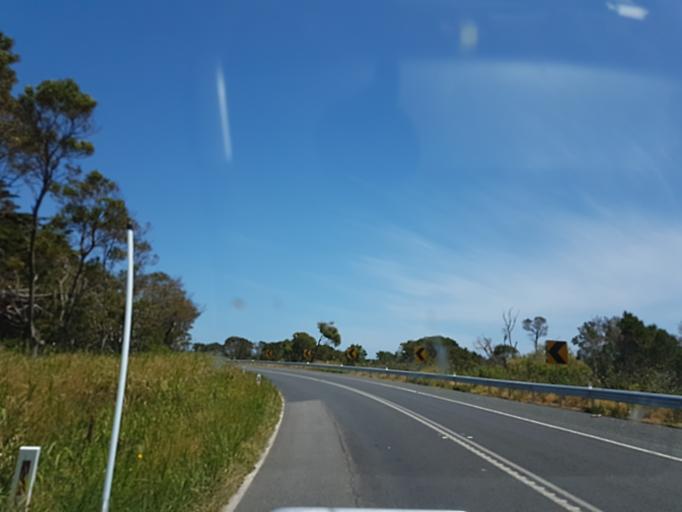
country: AU
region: Victoria
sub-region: Bass Coast
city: North Wonthaggi
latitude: -38.6980
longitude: 145.8554
